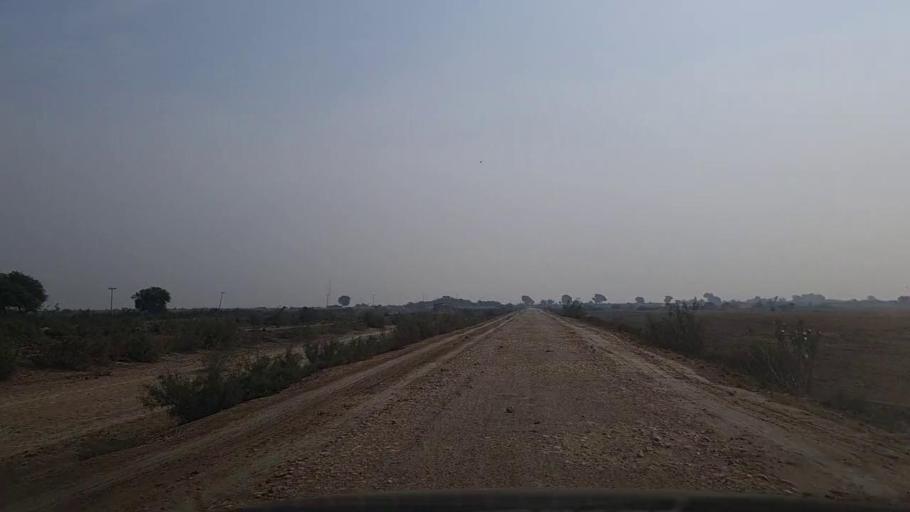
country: PK
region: Sindh
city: Mirpur Sakro
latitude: 24.3806
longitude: 67.7539
